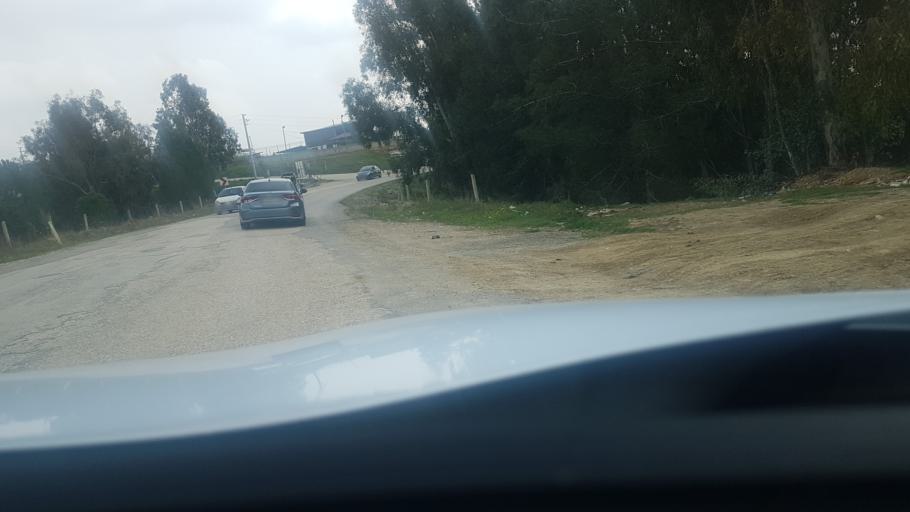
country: TR
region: Adana
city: Seyhan
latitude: 37.0606
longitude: 35.2571
